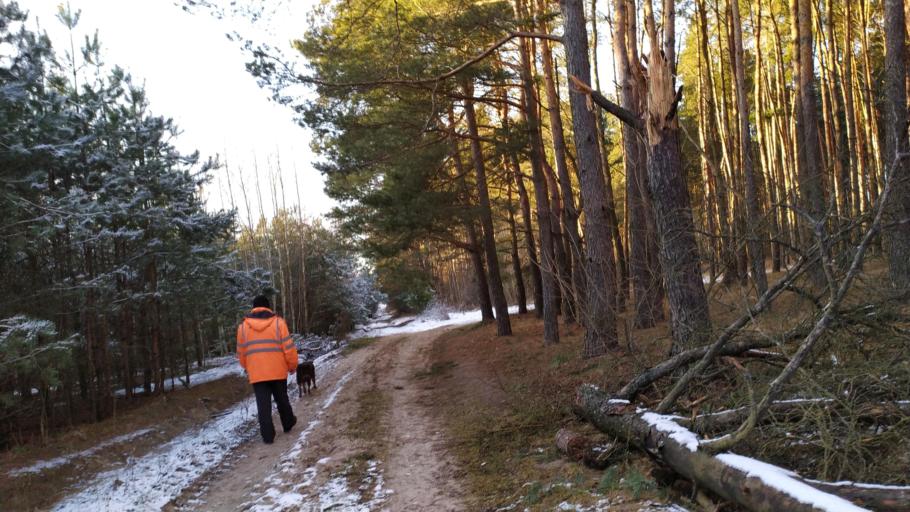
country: BY
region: Brest
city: Kamyanyets
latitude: 52.3840
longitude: 23.8310
